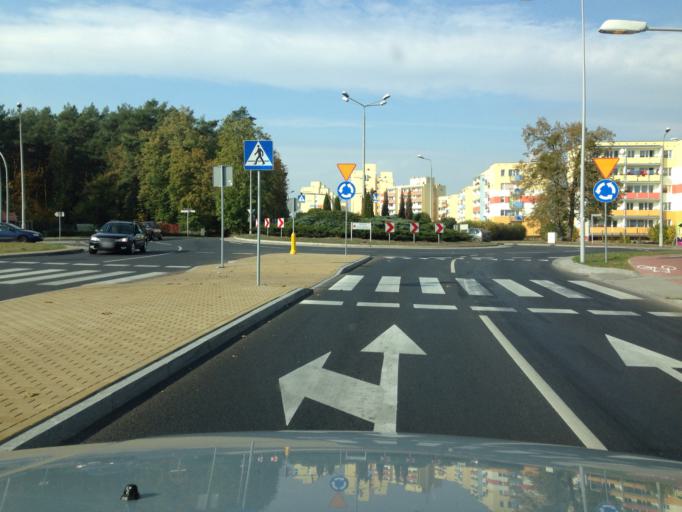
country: PL
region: Kujawsko-Pomorskie
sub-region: Grudziadz
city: Grudziadz
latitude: 53.4596
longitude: 18.7748
